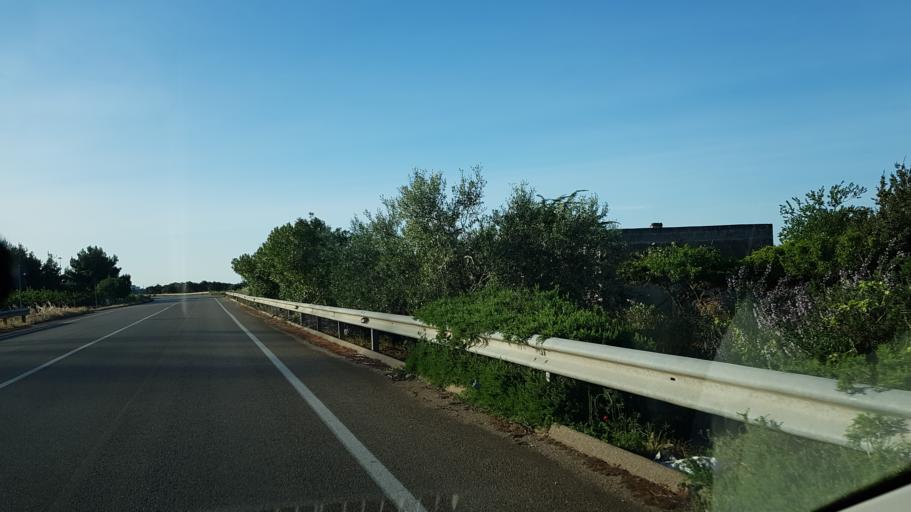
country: IT
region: Apulia
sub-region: Provincia di Brindisi
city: Mesagne
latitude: 40.5746
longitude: 17.8433
